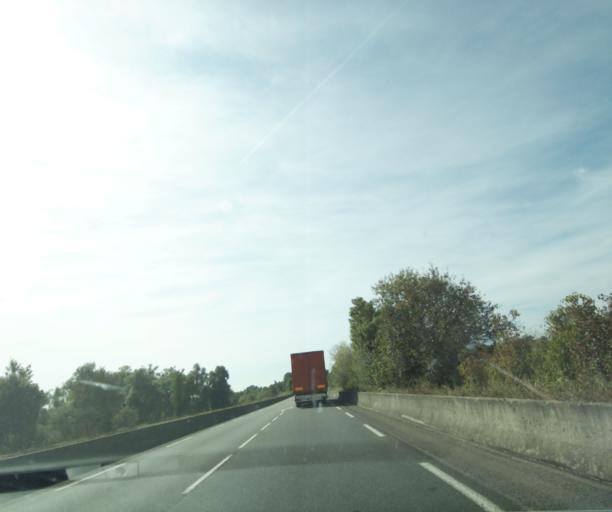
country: FR
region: Auvergne
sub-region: Departement de l'Allier
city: Saint-Remy-en-Rollat
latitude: 46.1856
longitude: 3.4043
